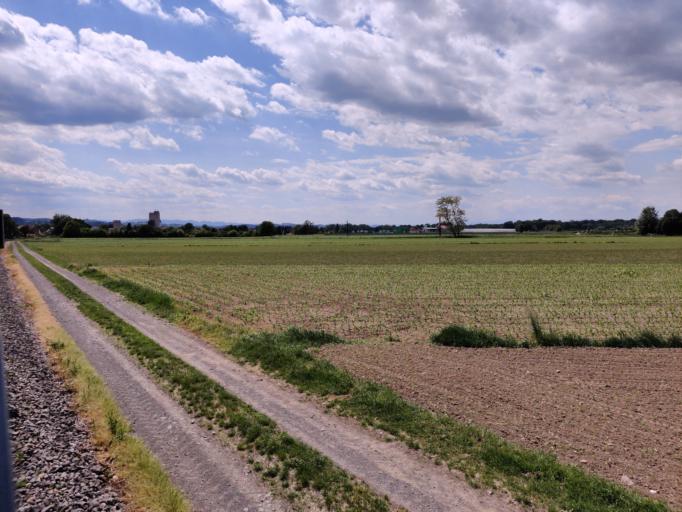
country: AT
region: Styria
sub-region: Politischer Bezirk Suedoststeiermark
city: Mureck
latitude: 46.7158
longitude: 15.7850
